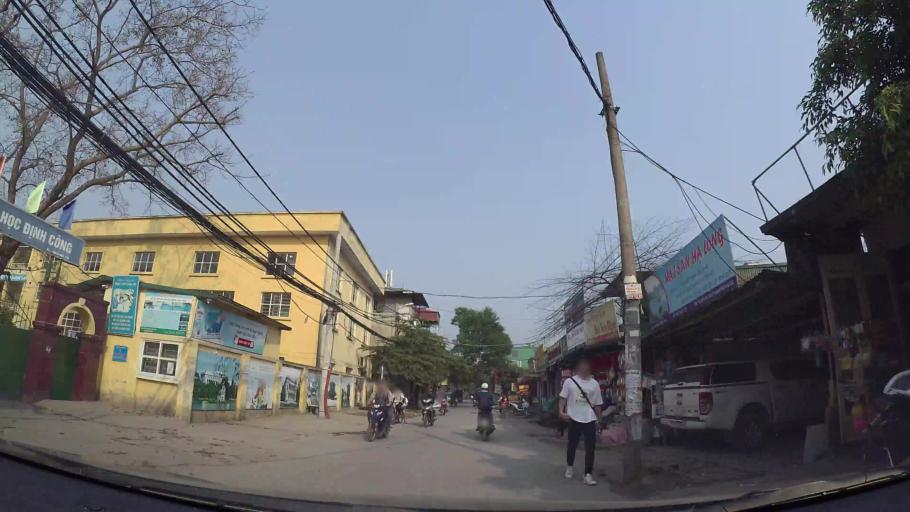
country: VN
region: Ha Noi
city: Thanh Xuan
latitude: 20.9831
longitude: 105.8266
